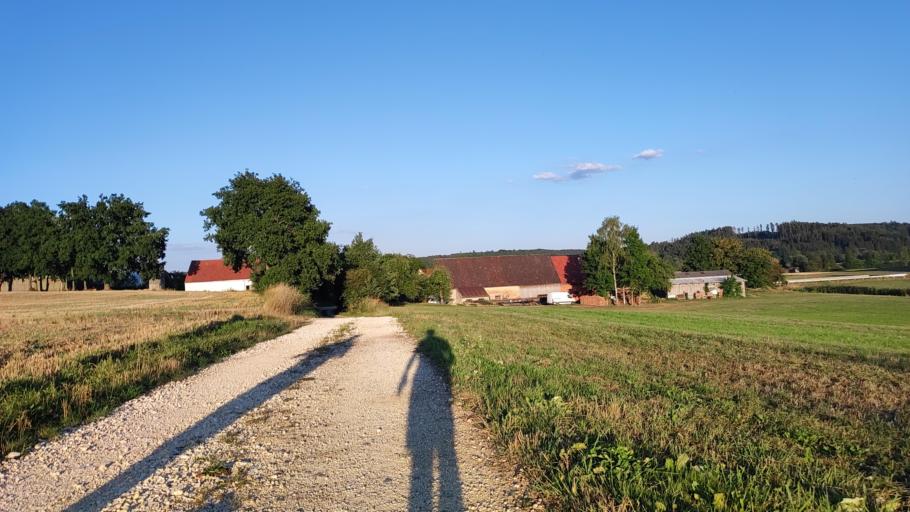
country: DE
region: Bavaria
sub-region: Swabia
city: Villenbach
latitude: 48.4983
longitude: 10.5984
